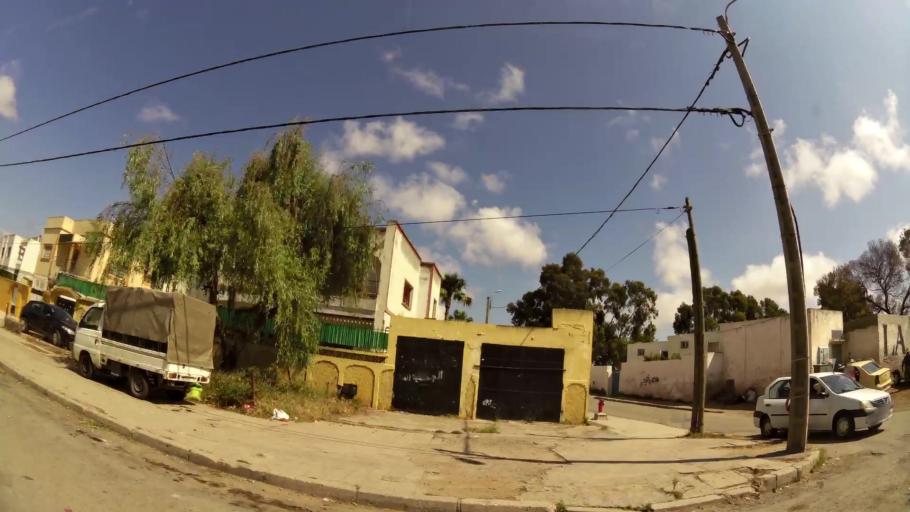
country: MA
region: Rabat-Sale-Zemmour-Zaer
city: Sale
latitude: 34.0380
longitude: -6.7961
